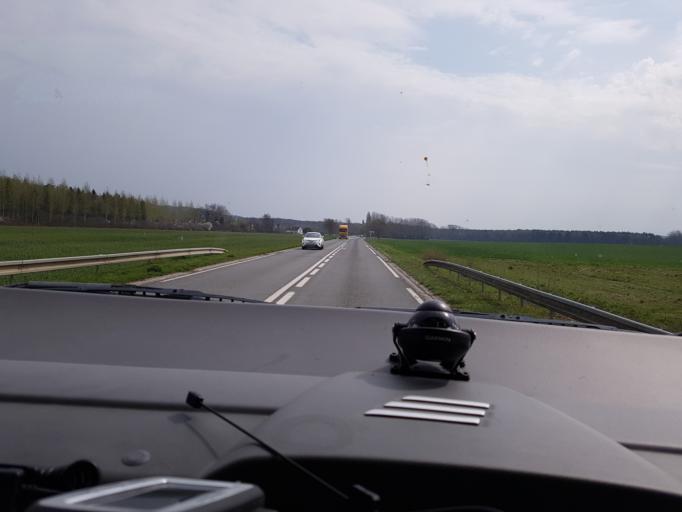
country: FR
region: Picardie
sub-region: Departement de l'Aisne
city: Coucy-le-Chateau-Auffrique
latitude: 49.5141
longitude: 3.3081
